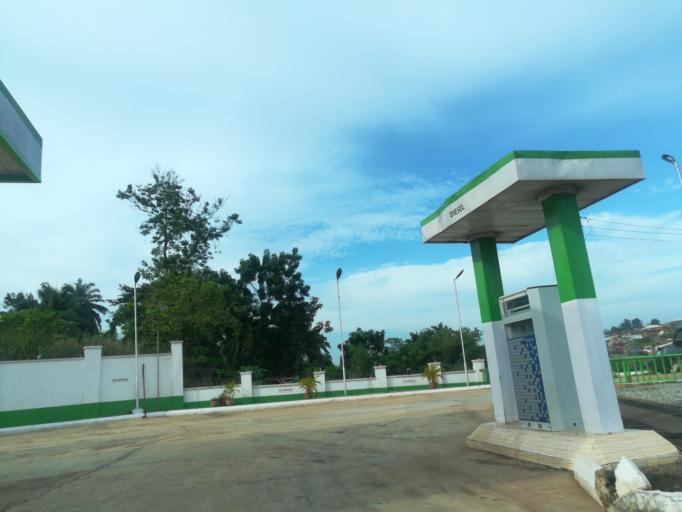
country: NG
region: Oyo
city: Ibadan
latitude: 7.3902
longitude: 3.9352
